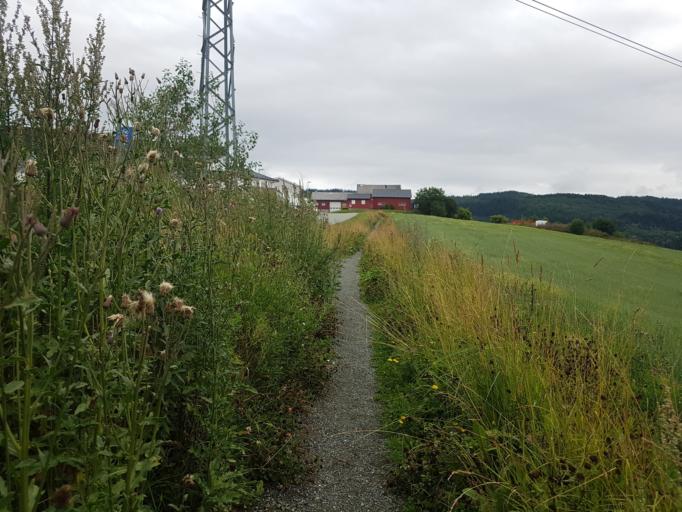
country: NO
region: Sor-Trondelag
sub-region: Trondheim
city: Trondheim
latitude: 63.3840
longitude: 10.4238
